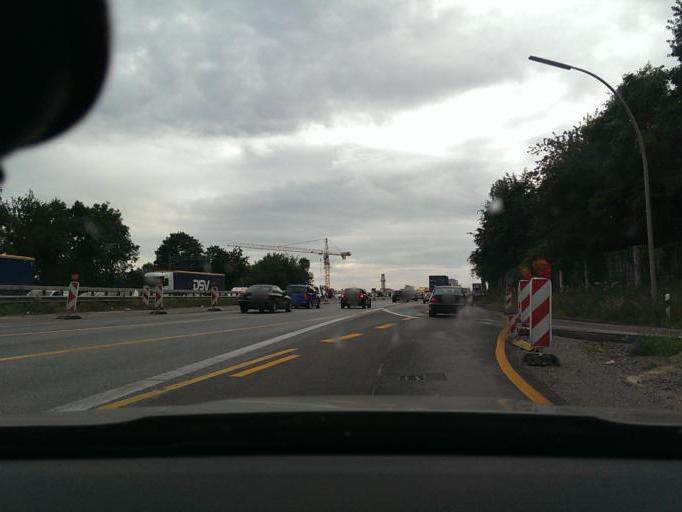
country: DE
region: Hamburg
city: Stellingen
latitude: 53.5936
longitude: 9.9215
